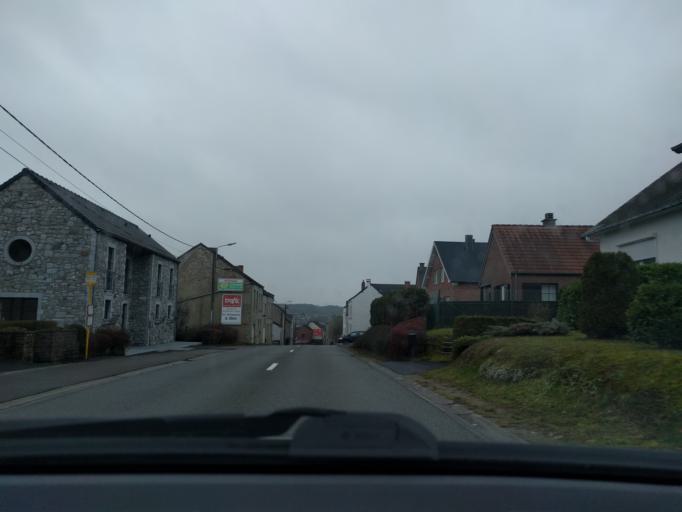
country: BE
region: Wallonia
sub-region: Province de Namur
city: Couvin
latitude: 50.0535
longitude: 4.5027
